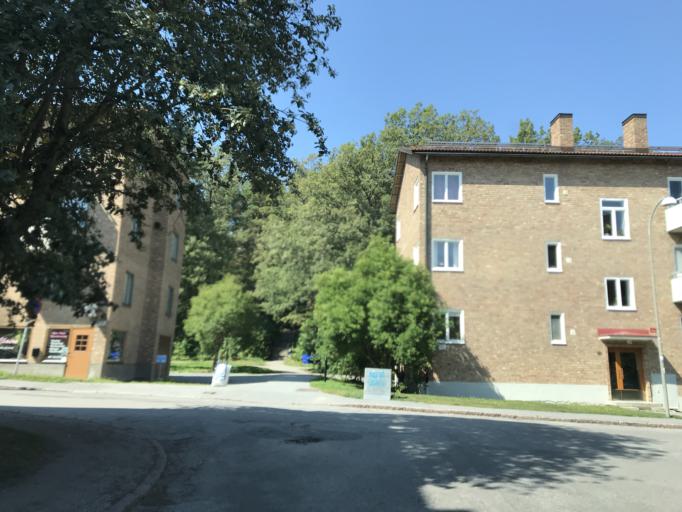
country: SE
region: Stockholm
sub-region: Stockholms Kommun
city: Bromma
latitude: 59.3361
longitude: 17.9494
